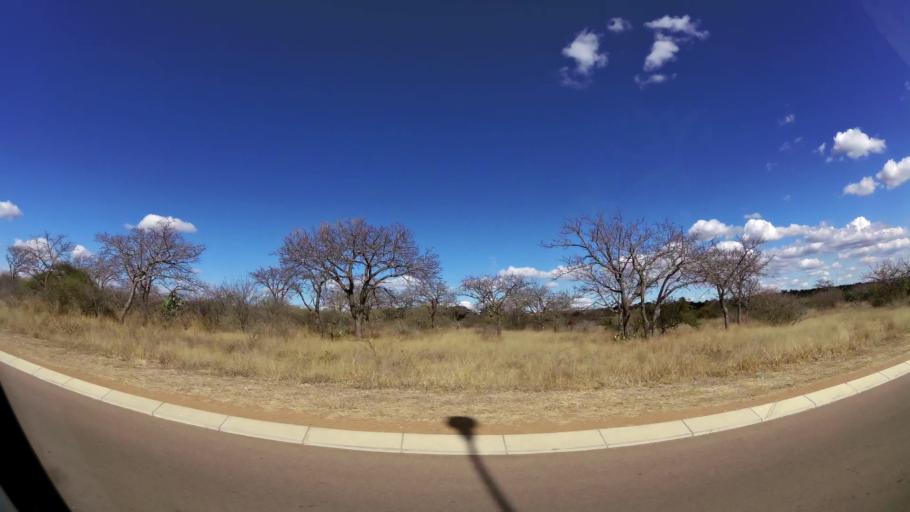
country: ZA
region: Limpopo
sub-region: Capricorn District Municipality
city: Polokwane
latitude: -23.8716
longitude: 29.4929
